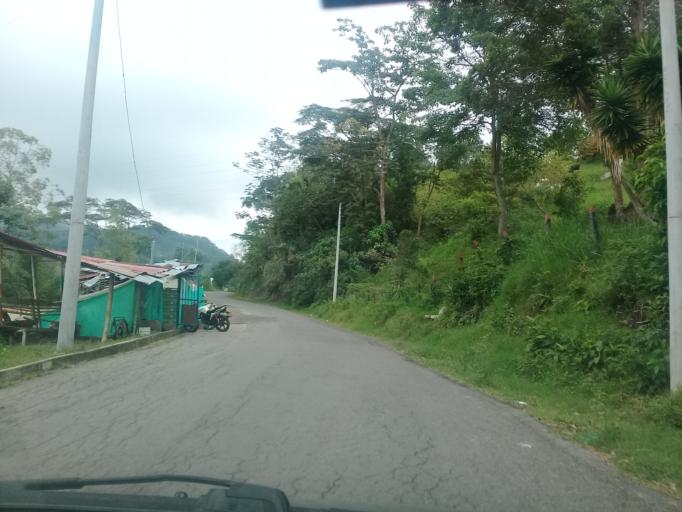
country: CO
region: Cundinamarca
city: Quipile
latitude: 4.7512
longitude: -74.5305
